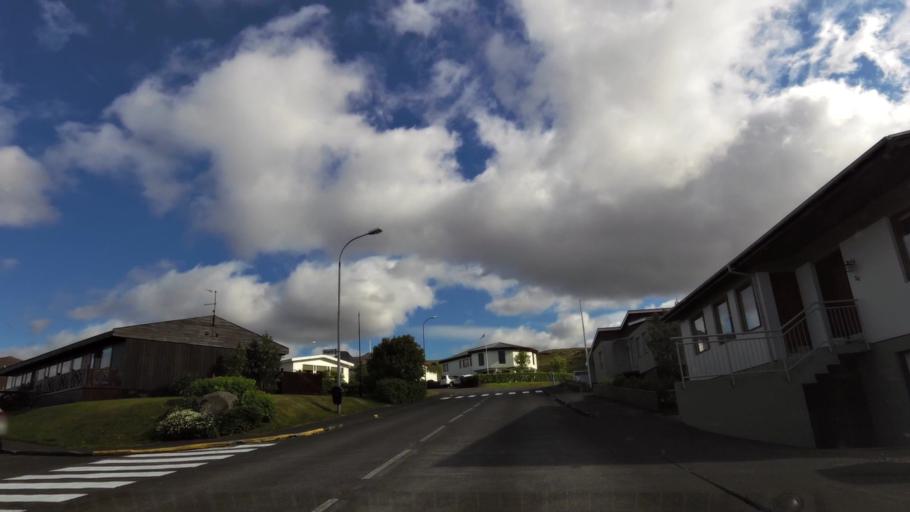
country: IS
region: West
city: Olafsvik
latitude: 64.8917
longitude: -23.7092
